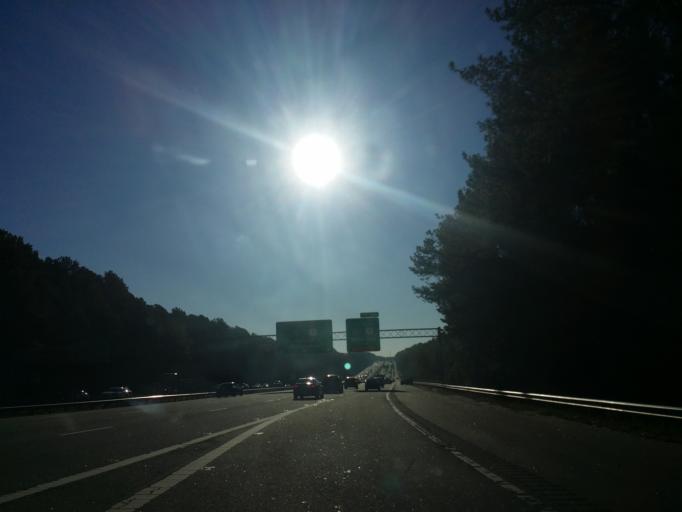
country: US
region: North Carolina
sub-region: Wake County
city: Cary
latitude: 35.8298
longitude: -78.7608
